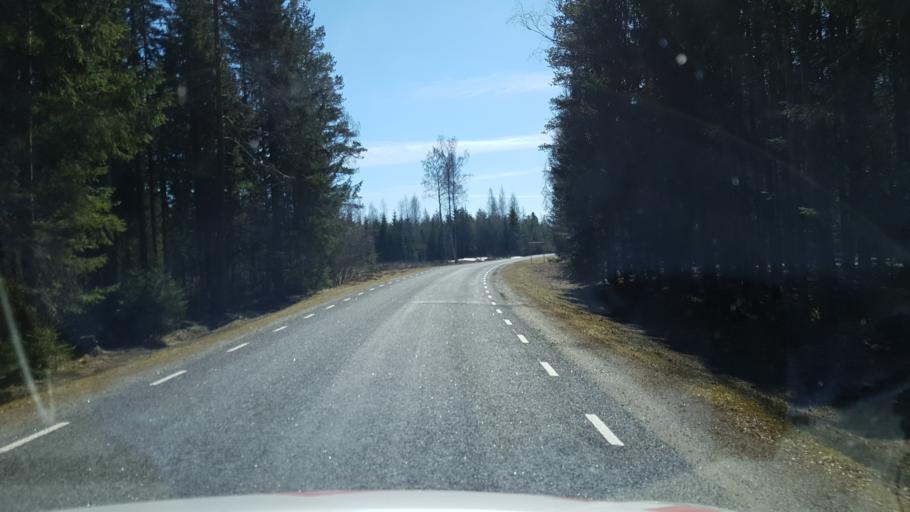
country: EE
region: Laeaene-Virumaa
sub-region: Vinni vald
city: Vinni
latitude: 59.1401
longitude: 26.5247
